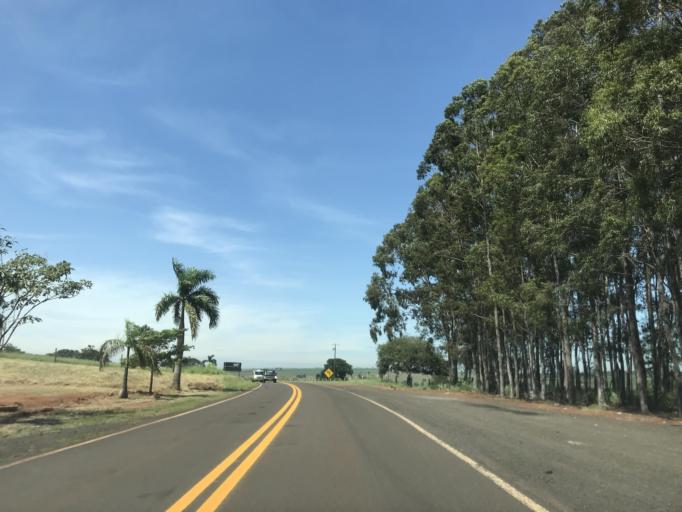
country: BR
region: Parana
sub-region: Terra Rica
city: Terra Rica
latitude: -22.7791
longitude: -52.6570
